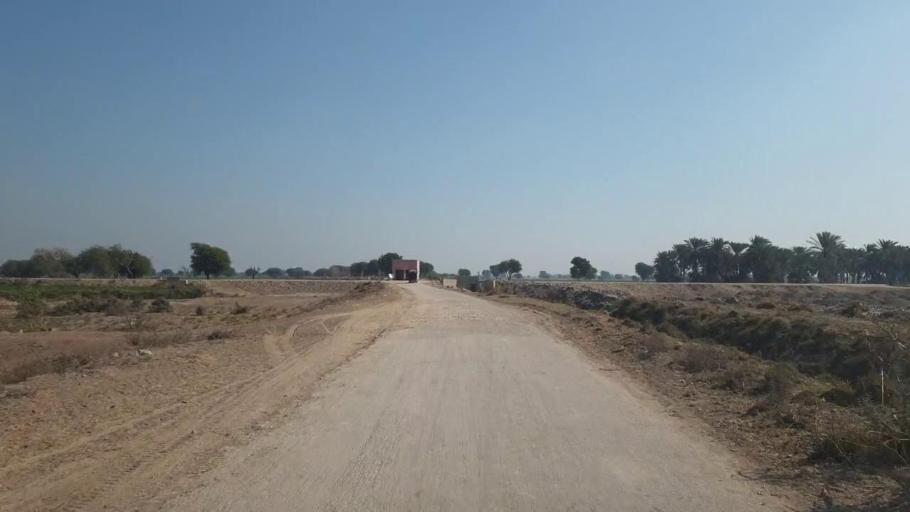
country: PK
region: Sindh
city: Shahdadpur
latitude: 25.9422
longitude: 68.6399
